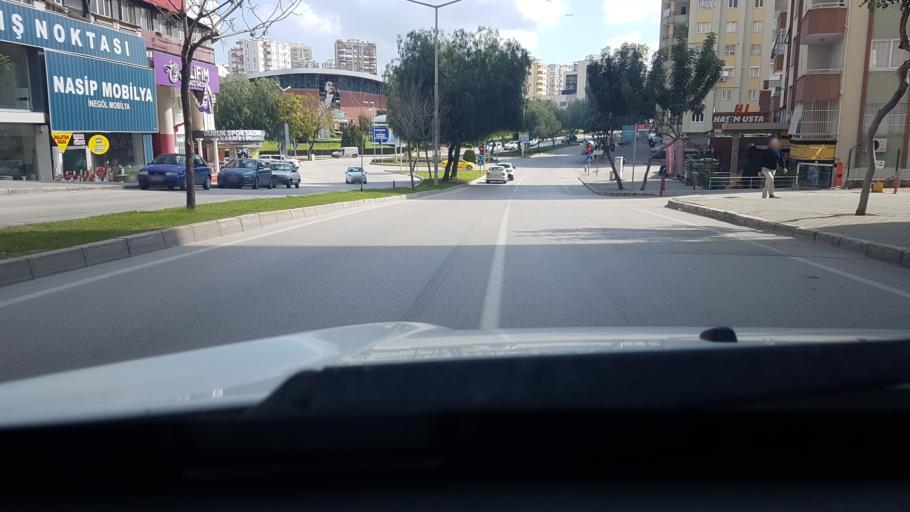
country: TR
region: Adana
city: Adana
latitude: 37.0356
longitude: 35.2935
